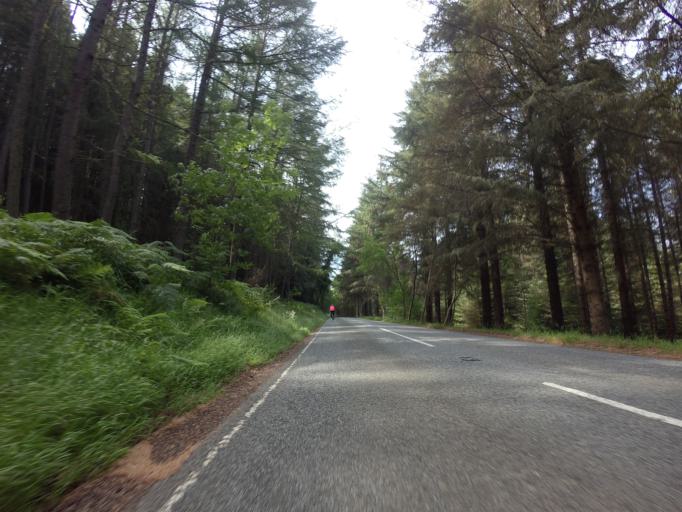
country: GB
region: Scotland
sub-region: Highland
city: Tain
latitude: 57.8270
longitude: -4.1376
